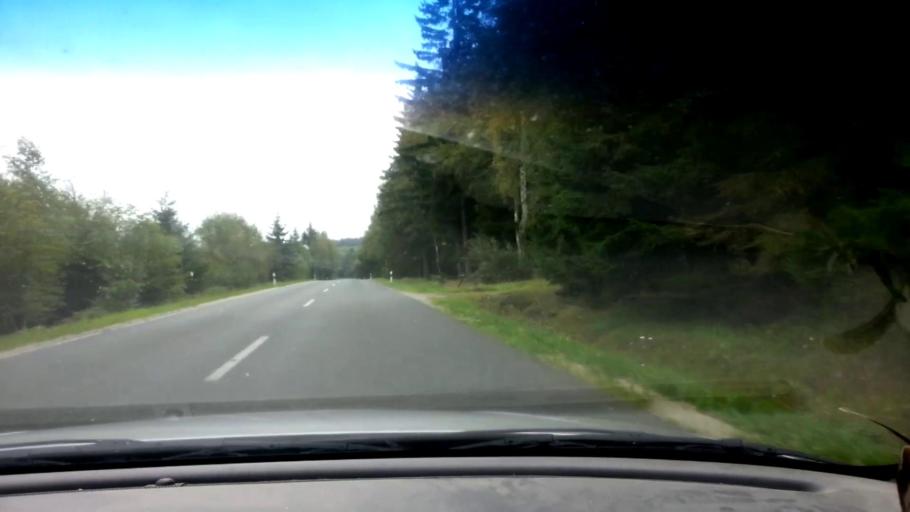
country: DE
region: Bavaria
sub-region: Upper Franconia
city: Grub
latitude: 50.0906
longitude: 11.9115
